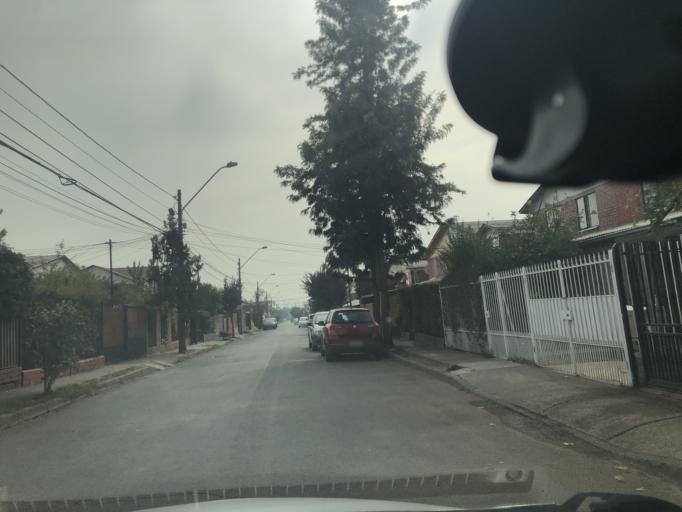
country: CL
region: Santiago Metropolitan
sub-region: Provincia de Cordillera
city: Puente Alto
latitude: -33.5661
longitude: -70.5647
